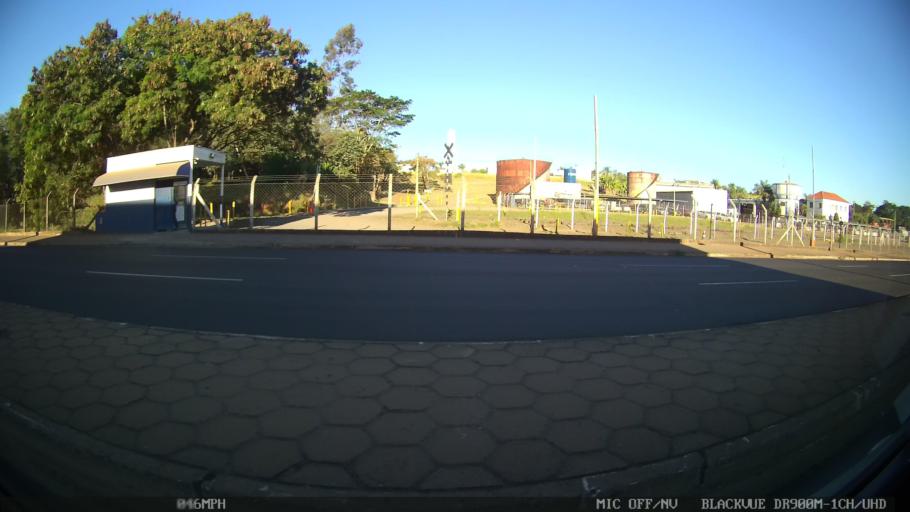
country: BR
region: Sao Paulo
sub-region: Araraquara
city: Araraquara
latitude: -21.7777
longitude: -48.1687
